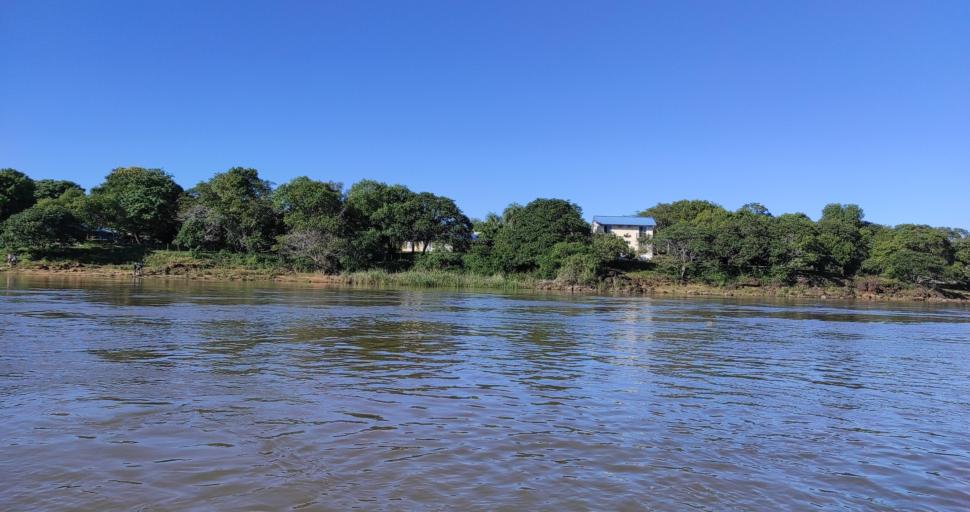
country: AR
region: Corrientes
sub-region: Departamento de Itati
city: Itati
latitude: -27.2647
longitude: -58.2693
